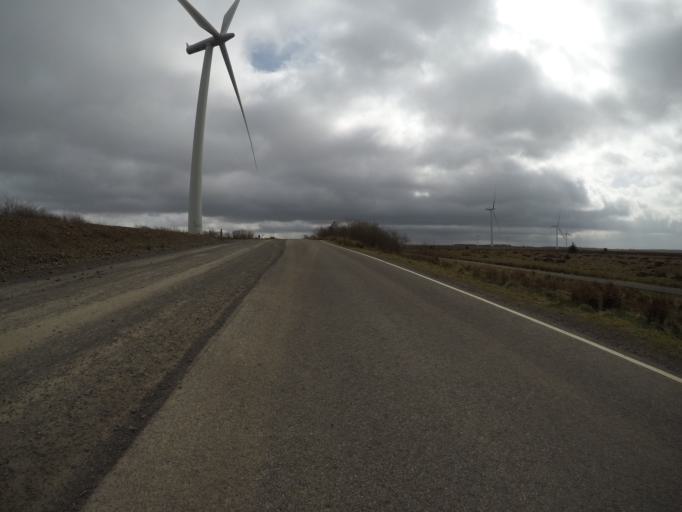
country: GB
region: Scotland
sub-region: East Renfrewshire
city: Newton Mearns
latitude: 55.7011
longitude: -4.3523
